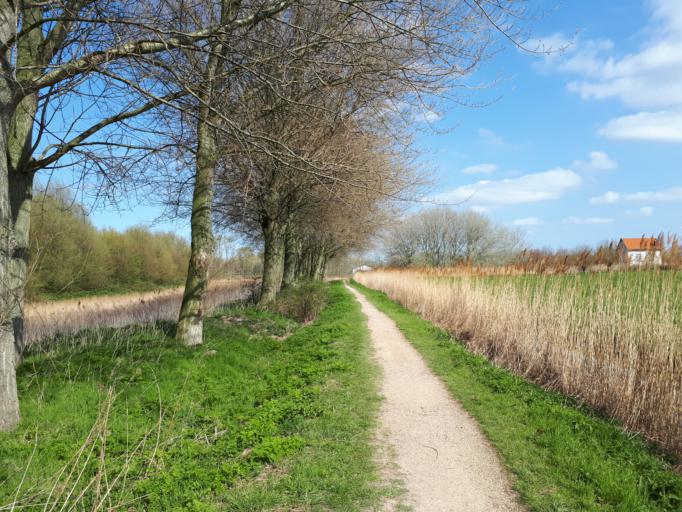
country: NL
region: South Holland
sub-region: Gemeente Pijnacker-Nootdorp
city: Pijnacker
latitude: 52.0220
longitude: 4.4037
